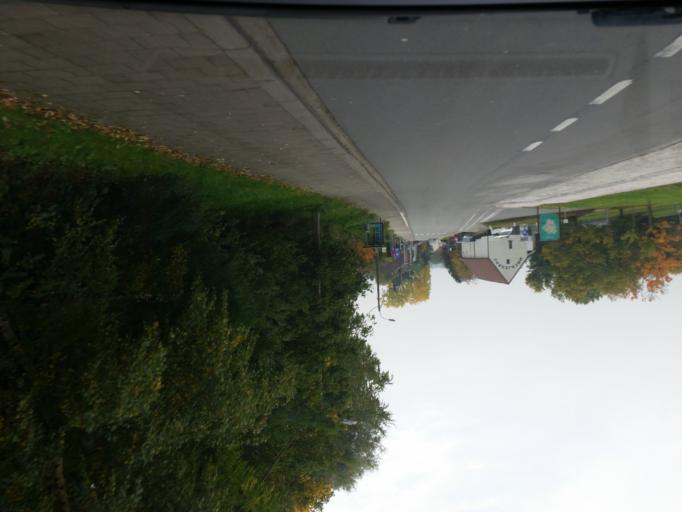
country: BE
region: Flanders
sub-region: Provincie Vlaams-Brabant
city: Drogenbos
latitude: 50.7740
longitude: 4.3165
